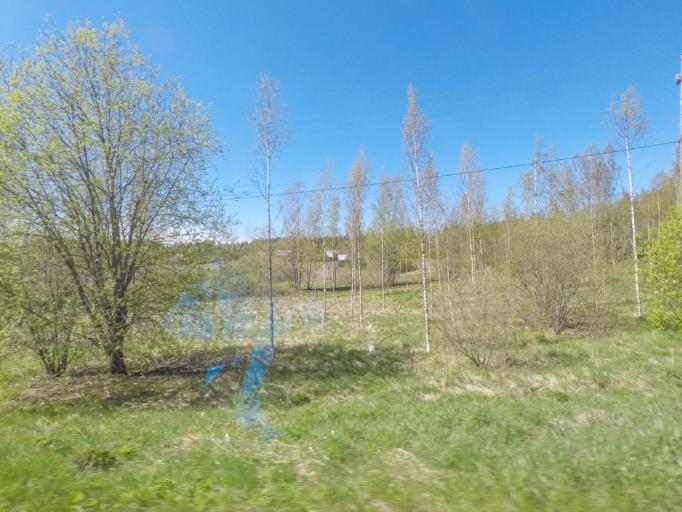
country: FI
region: Uusimaa
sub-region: Helsinki
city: Sammatti
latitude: 60.3637
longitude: 23.8045
